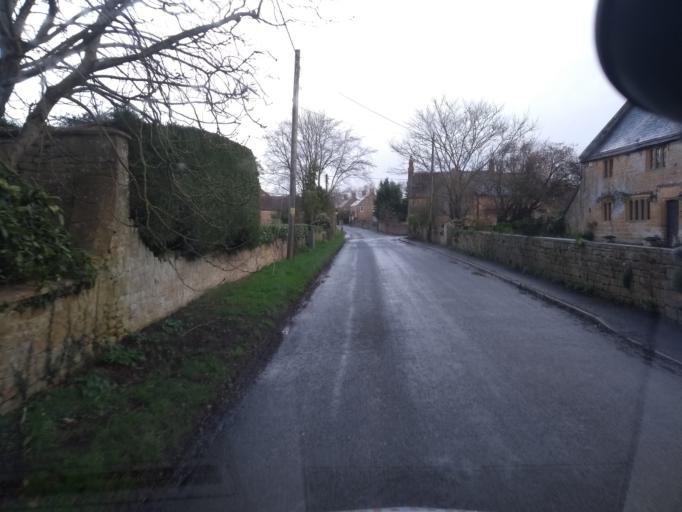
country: GB
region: England
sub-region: Somerset
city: Martock
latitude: 50.9802
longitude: -2.7815
